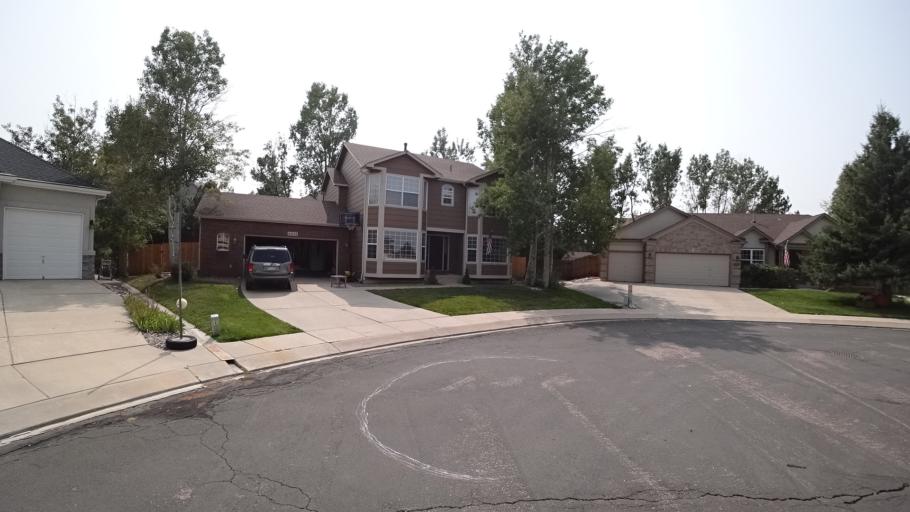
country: US
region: Colorado
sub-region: El Paso County
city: Cimarron Hills
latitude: 38.9167
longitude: -104.7469
